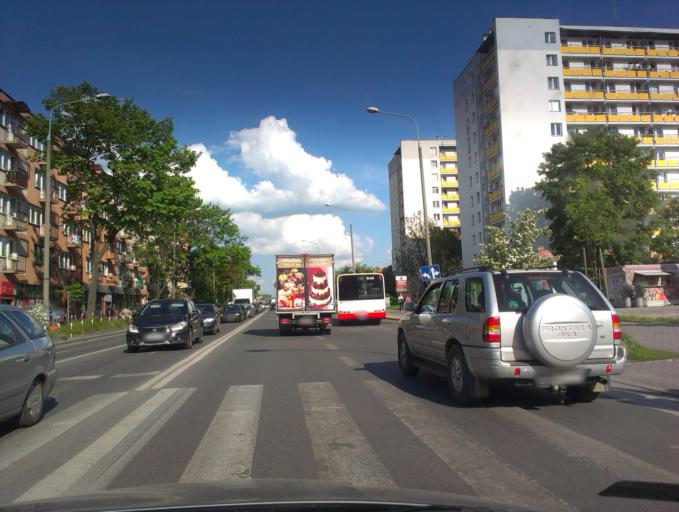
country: PL
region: Masovian Voivodeship
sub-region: Radom
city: Radom
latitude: 51.3997
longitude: 21.1673
